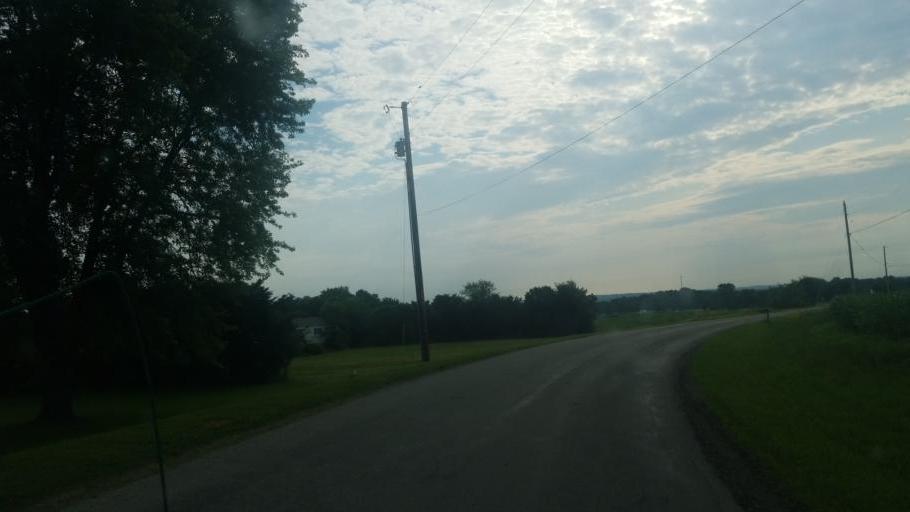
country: US
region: Ohio
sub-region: Wayne County
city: Wooster
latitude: 40.7980
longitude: -82.0299
